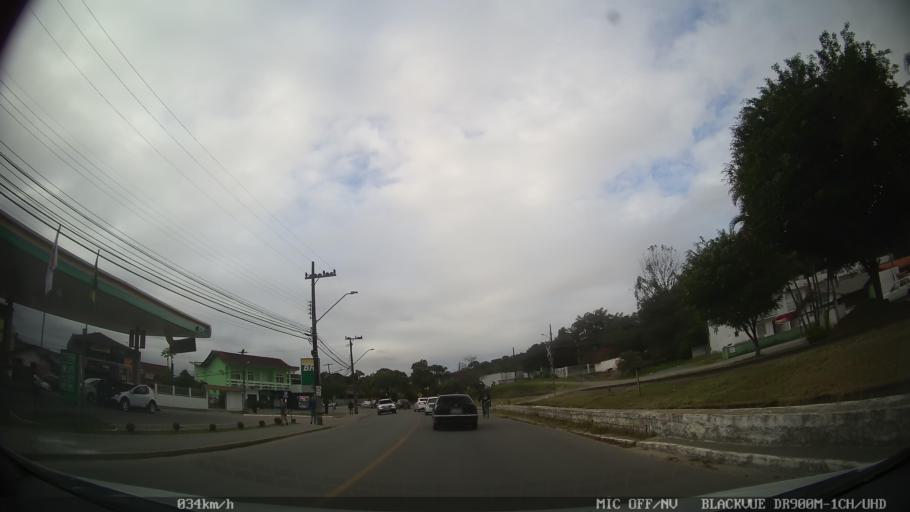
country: BR
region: Santa Catarina
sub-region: Joinville
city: Joinville
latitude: -26.3297
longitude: -48.8658
